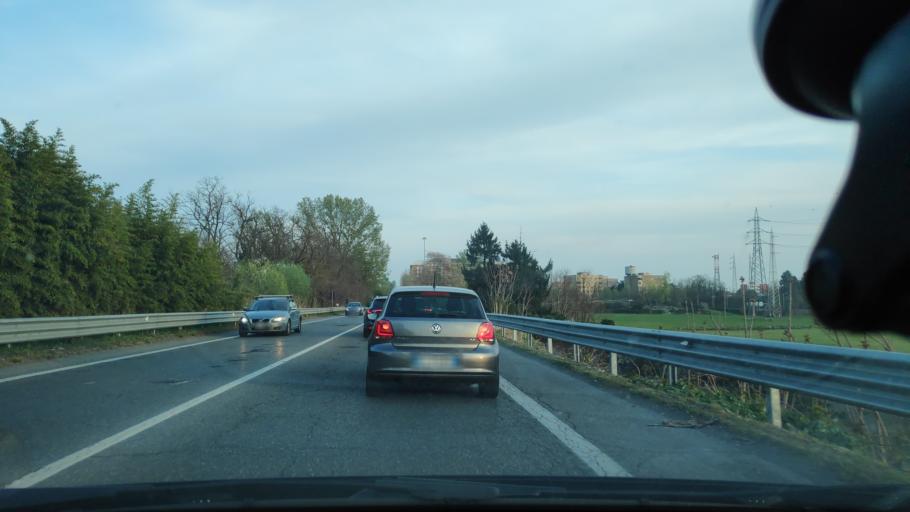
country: IT
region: Lombardy
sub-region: Citta metropolitana di Milano
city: Melegnano
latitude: 45.3672
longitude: 9.3170
